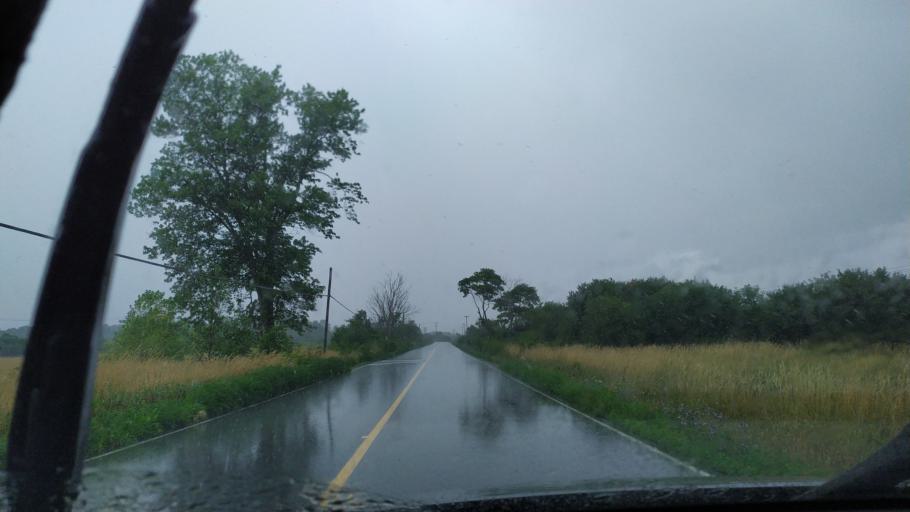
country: CA
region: Ontario
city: Prince Edward
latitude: 43.9715
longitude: -77.3905
